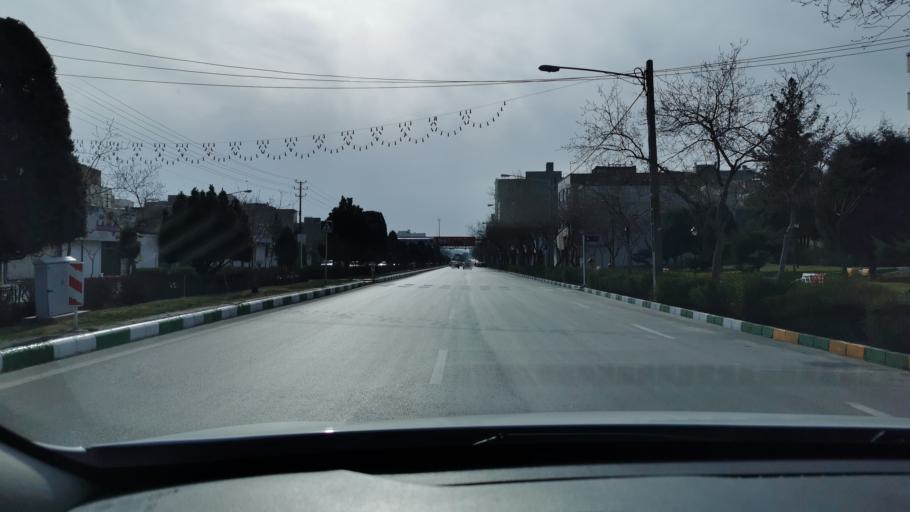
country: IR
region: Razavi Khorasan
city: Mashhad
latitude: 36.2980
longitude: 59.5259
